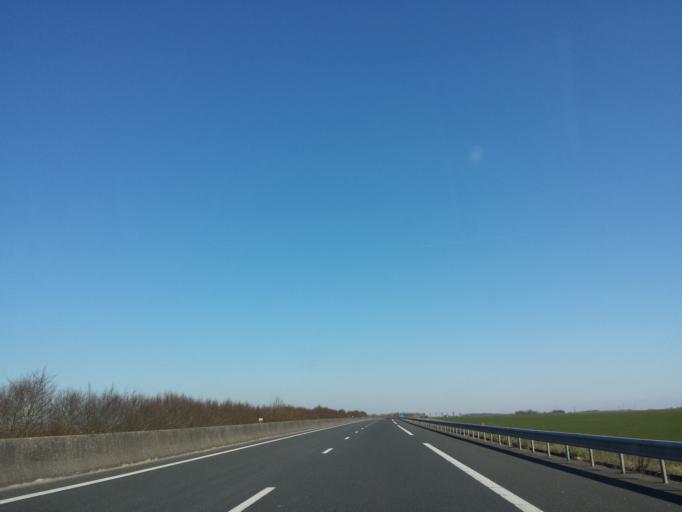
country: FR
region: Picardie
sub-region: Departement de l'Oise
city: Tille
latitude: 49.5067
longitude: 2.1777
